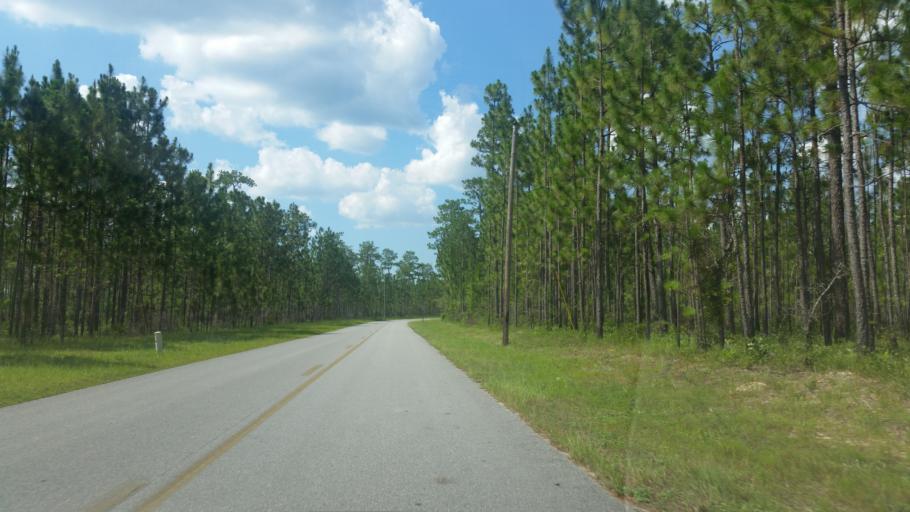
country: US
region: Florida
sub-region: Santa Rosa County
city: East Milton
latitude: 30.6899
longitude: -86.8761
